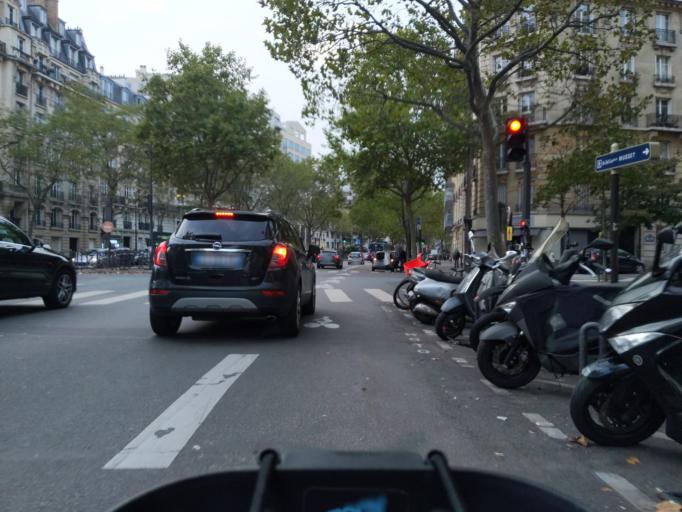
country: FR
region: Ile-de-France
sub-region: Departement des Hauts-de-Seine
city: Boulogne-Billancourt
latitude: 48.8431
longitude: 2.2605
